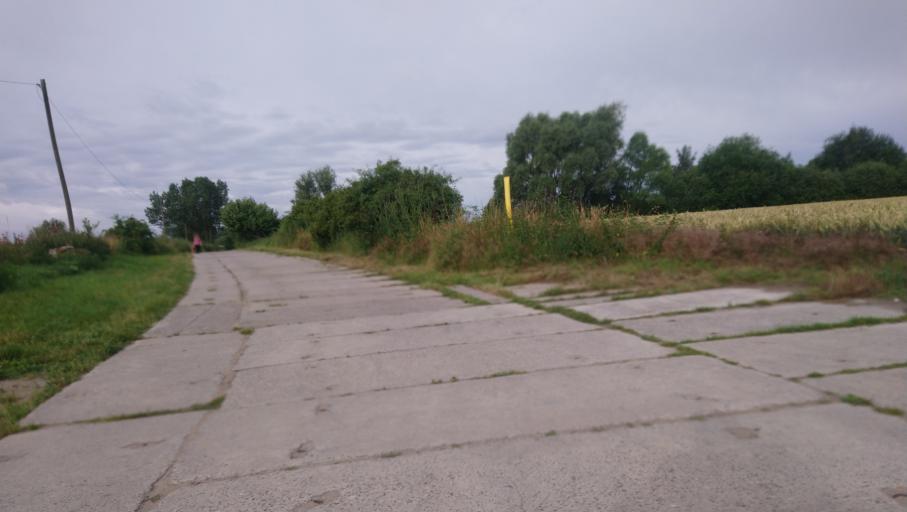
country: DE
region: Mecklenburg-Vorpommern
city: Papendorf
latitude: 54.0584
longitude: 12.0966
